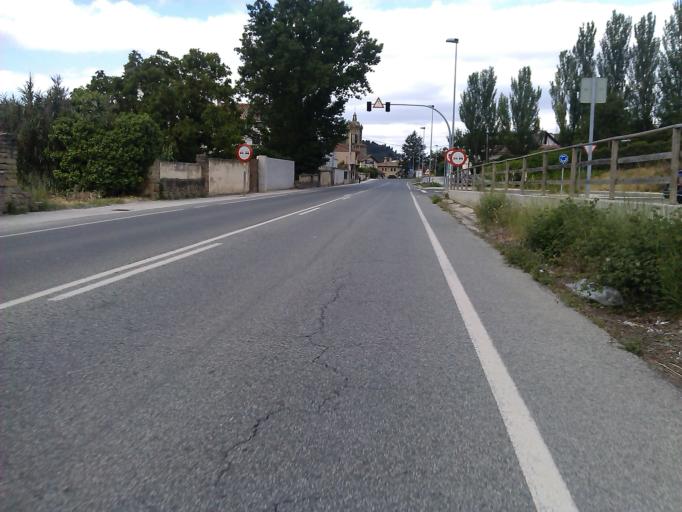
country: ES
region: Navarre
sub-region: Provincia de Navarra
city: Puente la Reina
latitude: 42.6749
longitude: -1.8086
